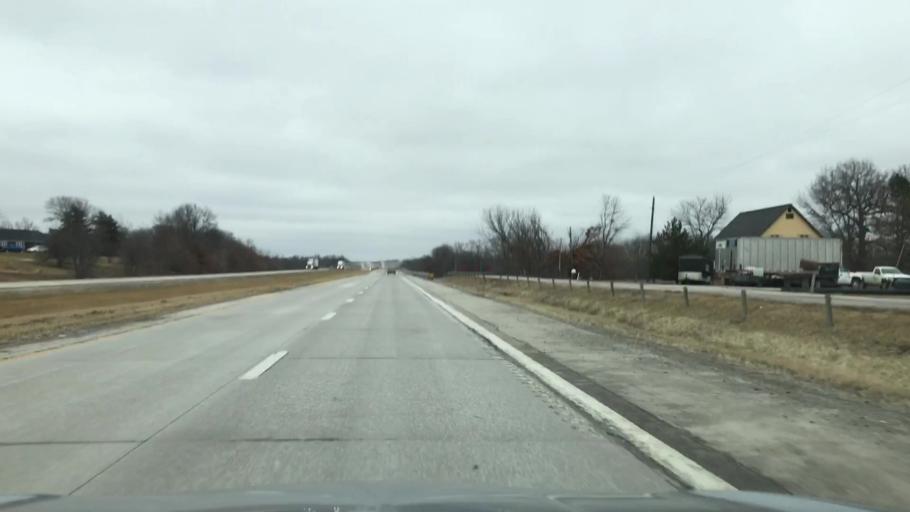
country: US
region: Missouri
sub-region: Linn County
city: Marceline
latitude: 39.7616
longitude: -92.9882
